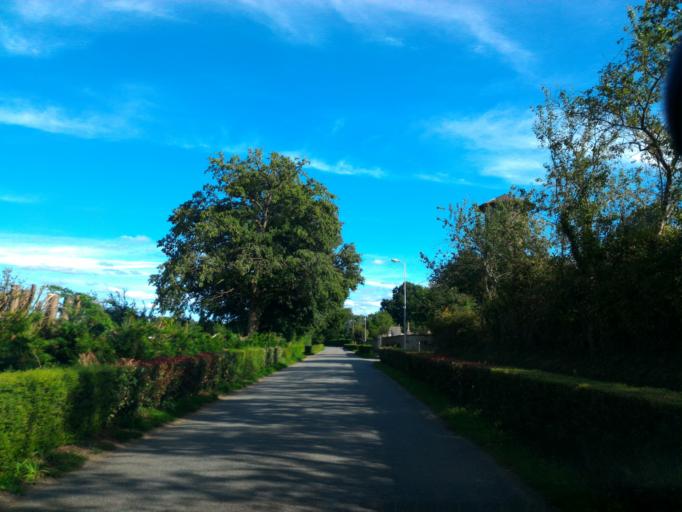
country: FR
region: Poitou-Charentes
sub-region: Departement de la Charente
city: Brigueuil
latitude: 46.0015
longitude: 0.8524
